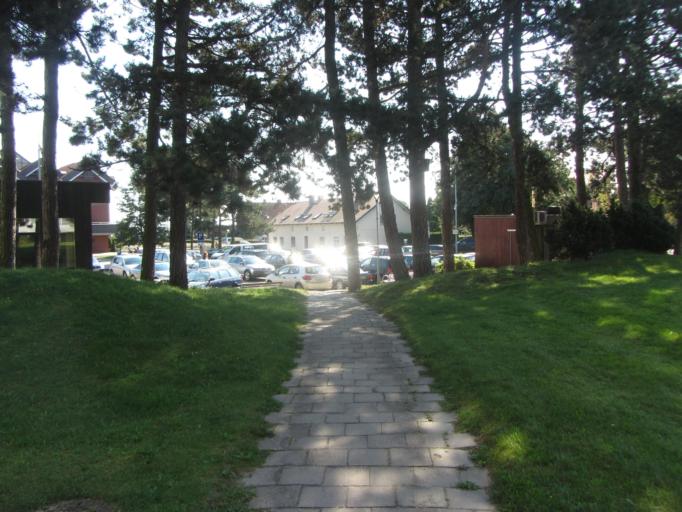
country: LT
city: Nida
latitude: 55.3041
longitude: 21.0049
